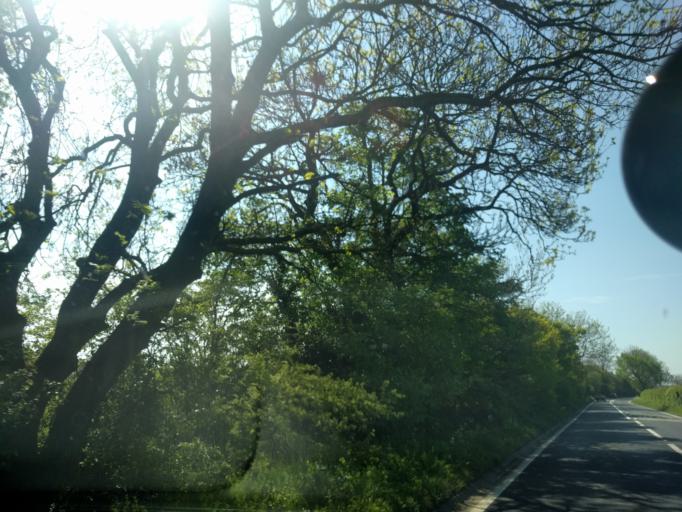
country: GB
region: England
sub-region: Somerset
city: Ilchester
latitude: 51.0544
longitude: -2.6442
